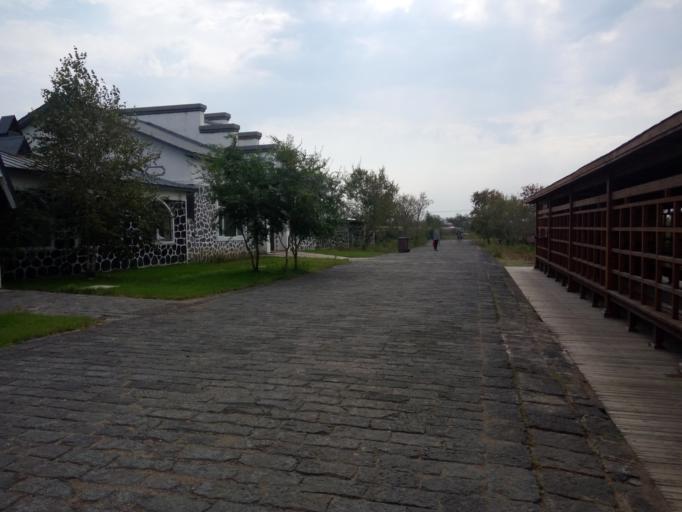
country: CN
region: Heilongjiang Sheng
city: Erjing
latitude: 48.6457
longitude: 126.1492
